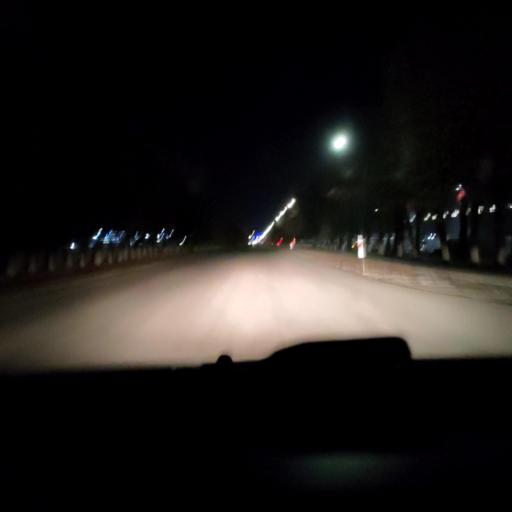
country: RU
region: Voronezj
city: Podgornoye
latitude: 51.8023
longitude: 39.2110
